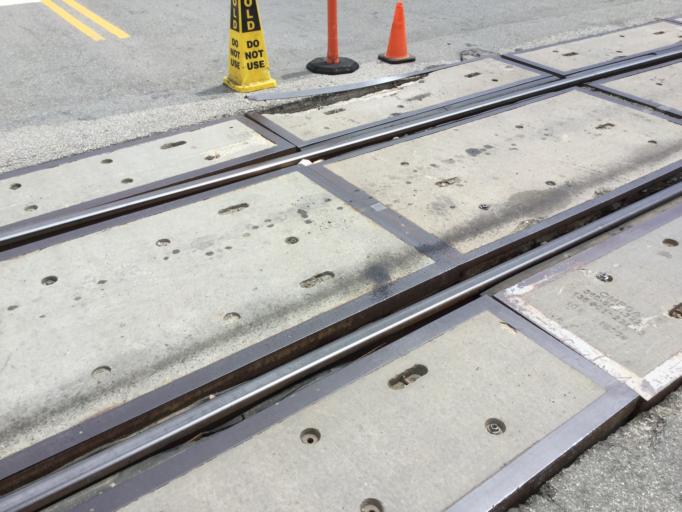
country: US
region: Kansas
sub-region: Johnson County
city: Lenexa
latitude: 38.9510
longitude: -94.7483
